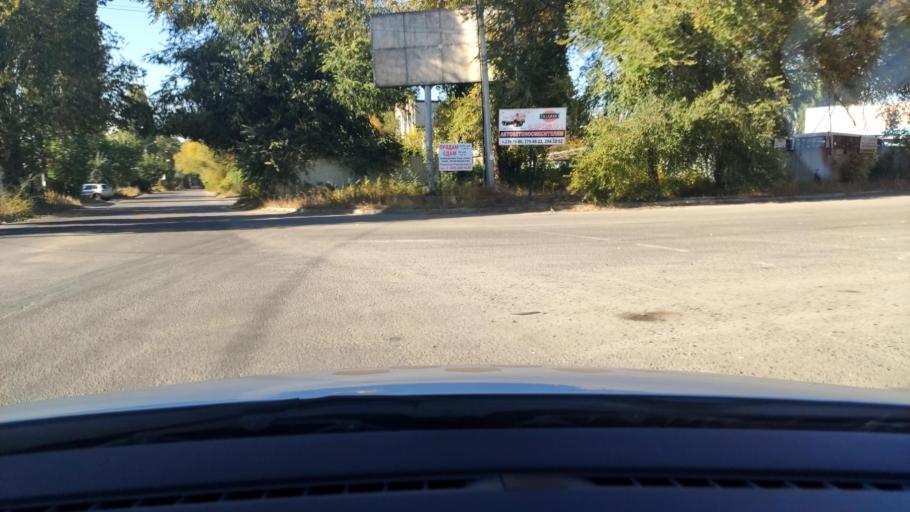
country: RU
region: Voronezj
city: Voronezh
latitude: 51.6817
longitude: 39.1473
